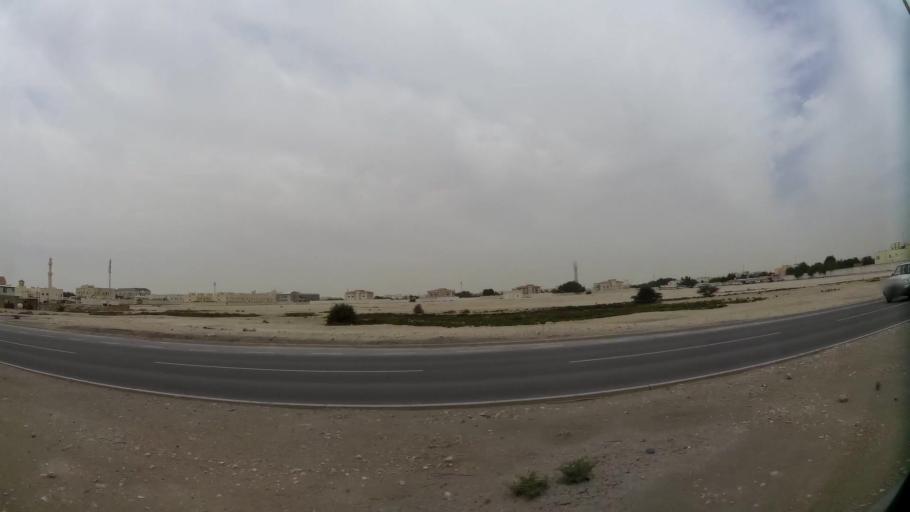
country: QA
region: Baladiyat ar Rayyan
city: Ar Rayyan
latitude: 25.2295
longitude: 51.4625
